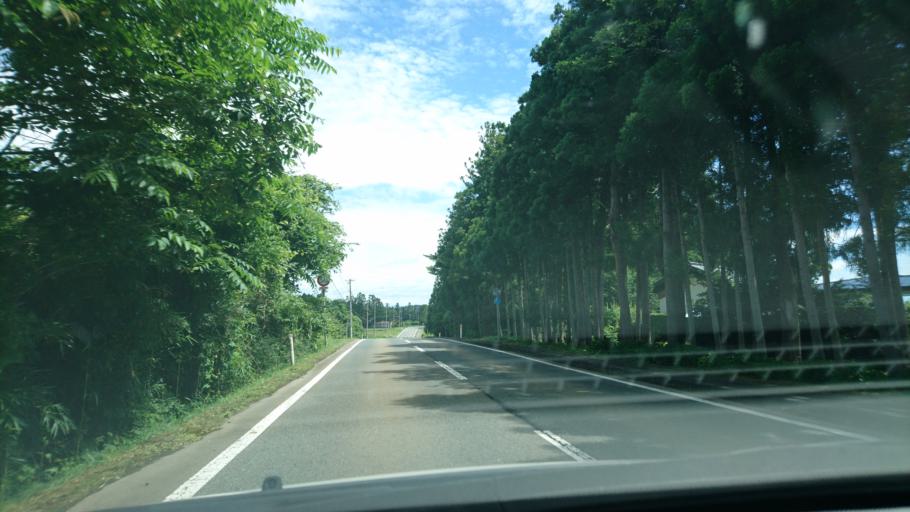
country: JP
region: Iwate
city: Hanamaki
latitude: 39.4178
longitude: 141.1739
